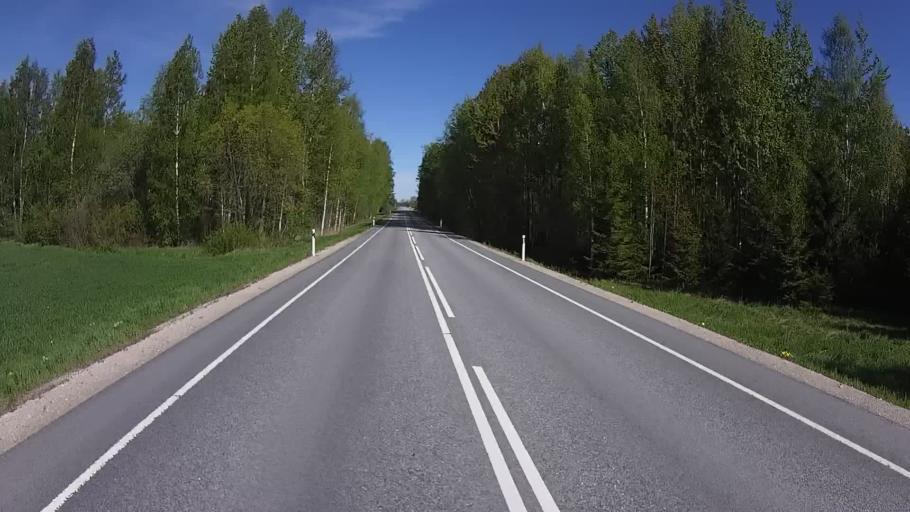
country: EE
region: Polvamaa
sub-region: Raepina vald
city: Rapina
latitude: 58.0597
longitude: 27.5506
